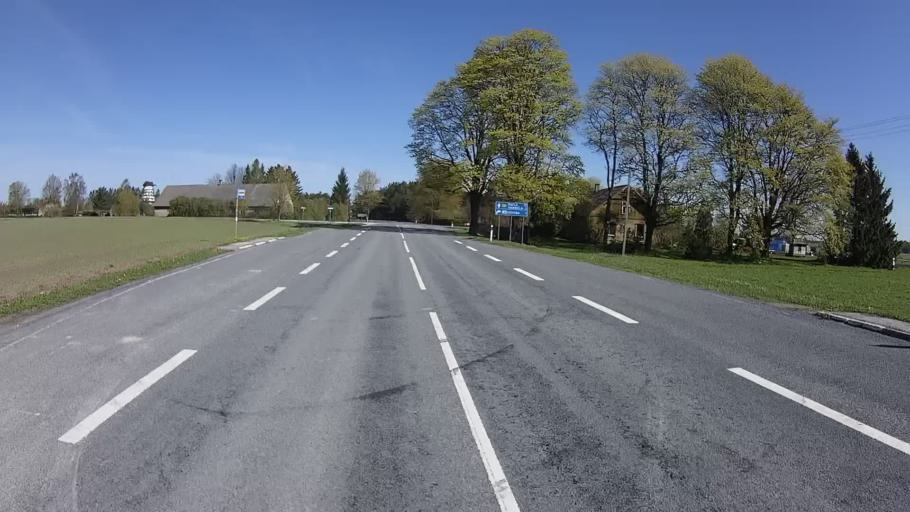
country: EE
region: Raplamaa
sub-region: Kehtna vald
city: Kehtna
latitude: 58.8997
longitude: 24.7878
